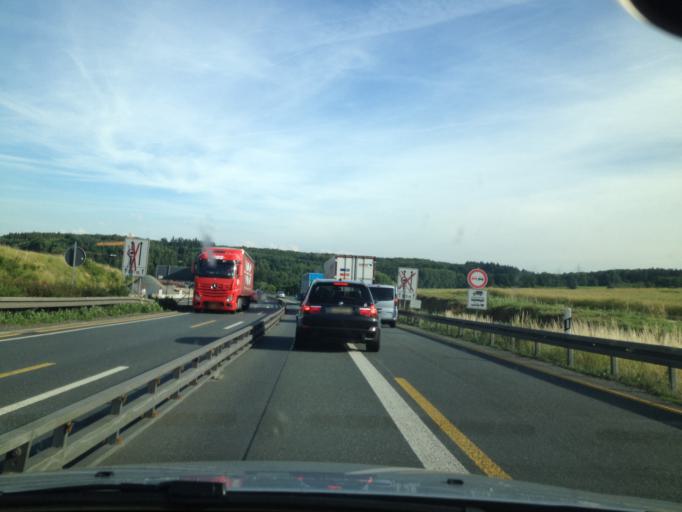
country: DE
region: Hesse
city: Allendorf an der Lahn
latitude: 50.5515
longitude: 8.5648
